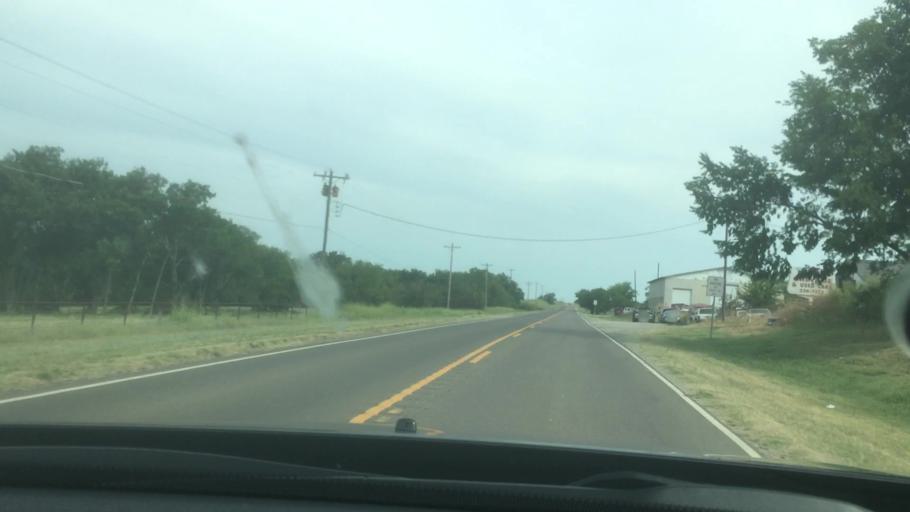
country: US
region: Oklahoma
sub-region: Garvin County
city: Pauls Valley
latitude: 34.7465
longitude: -97.2833
